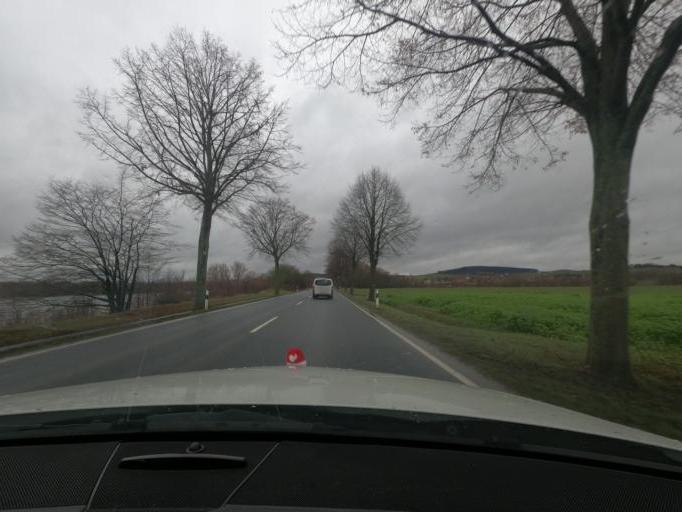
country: DE
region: Lower Saxony
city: Northeim
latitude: 51.7410
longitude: 9.9704
